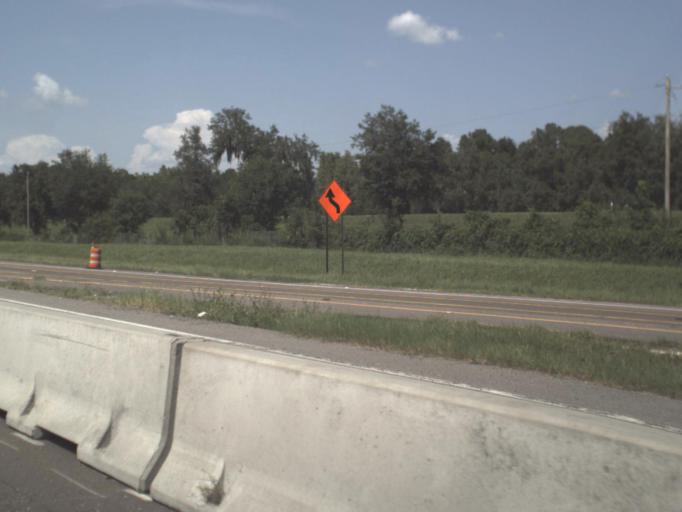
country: US
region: Florida
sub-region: Hillsborough County
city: Thonotosassa
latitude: 28.0784
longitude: -82.3529
